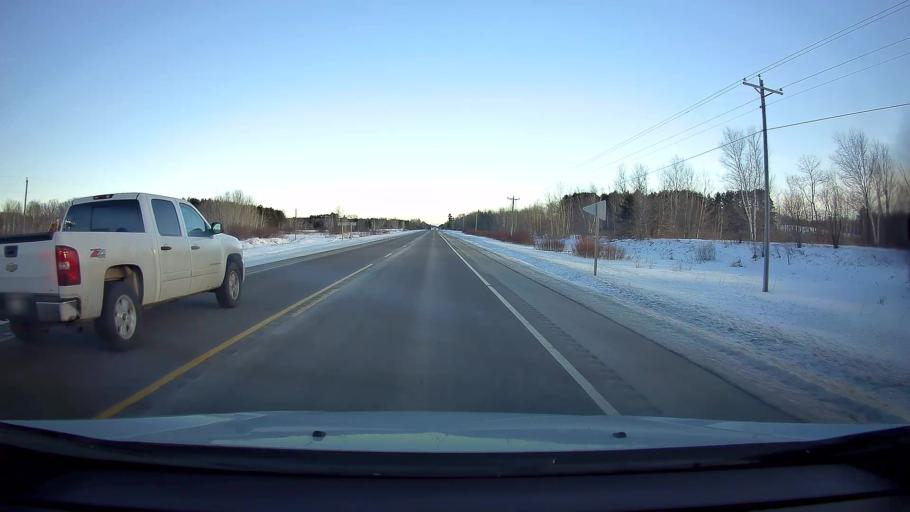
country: US
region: Wisconsin
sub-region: Washburn County
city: Shell Lake
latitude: 45.7121
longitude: -91.9430
